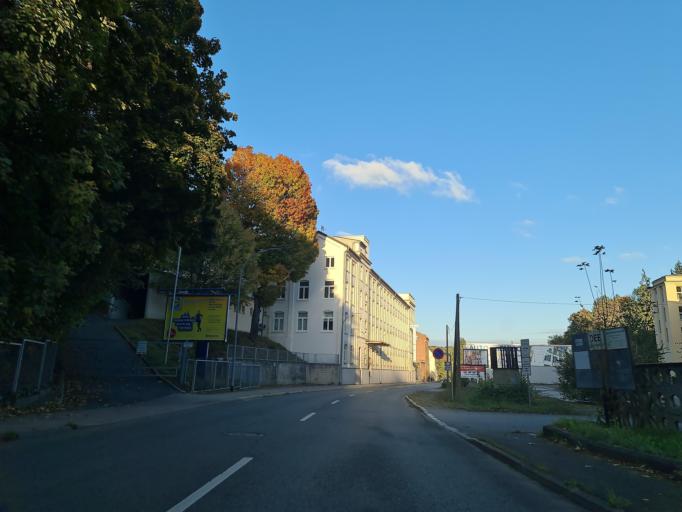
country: DE
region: Thuringia
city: Greiz
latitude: 50.6559
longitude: 12.1806
